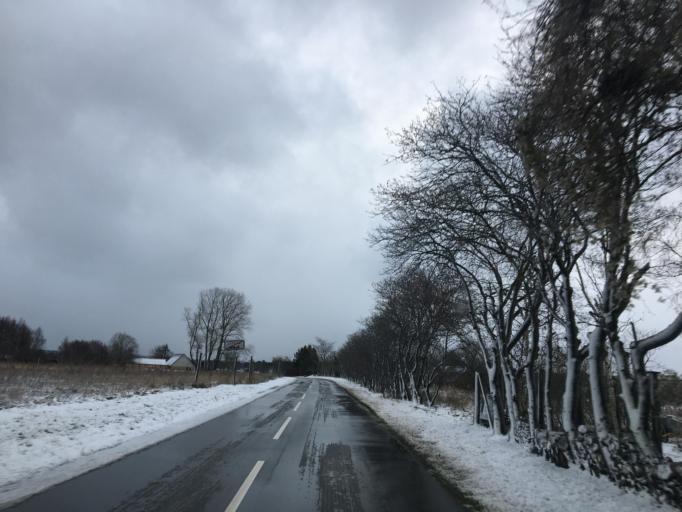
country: DK
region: Zealand
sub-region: Odsherred Kommune
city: Asnaes
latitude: 55.8363
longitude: 11.5579
